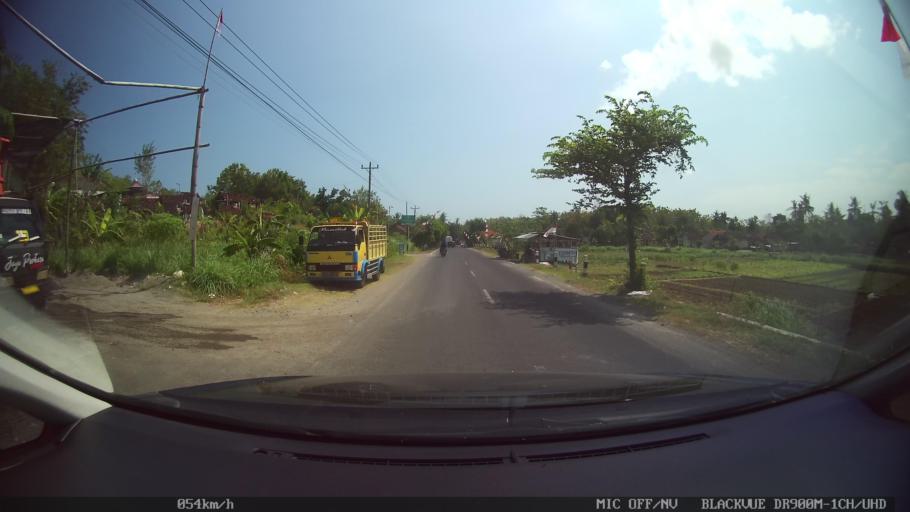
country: ID
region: Daerah Istimewa Yogyakarta
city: Pundong
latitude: -7.9875
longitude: 110.3227
